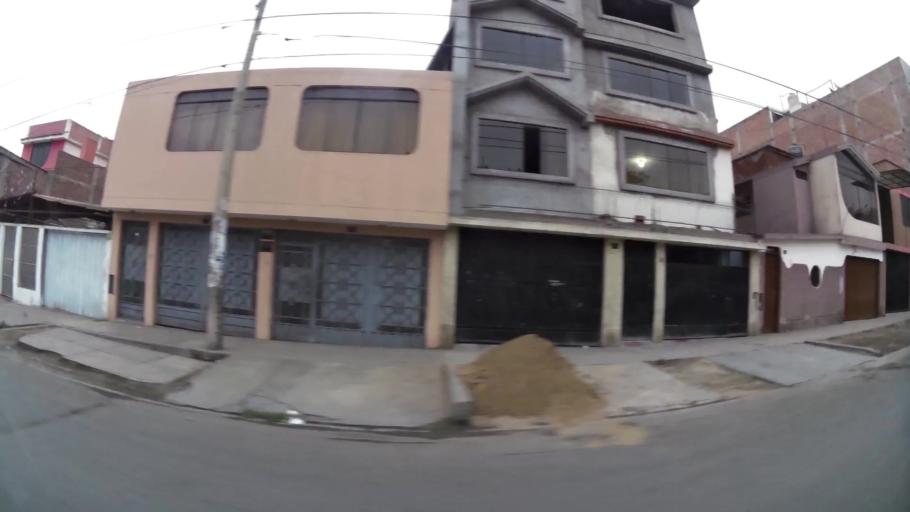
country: PE
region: Lima
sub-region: Lima
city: Vitarte
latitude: -12.0110
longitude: -76.9822
